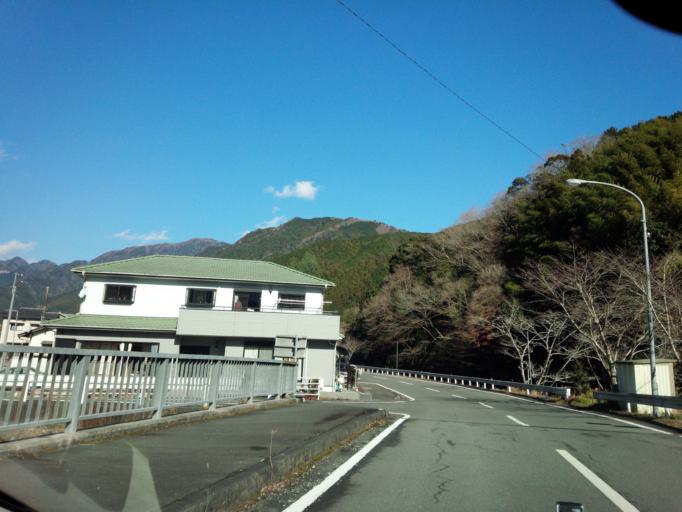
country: JP
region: Shizuoka
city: Shizuoka-shi
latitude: 35.1350
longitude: 138.4336
